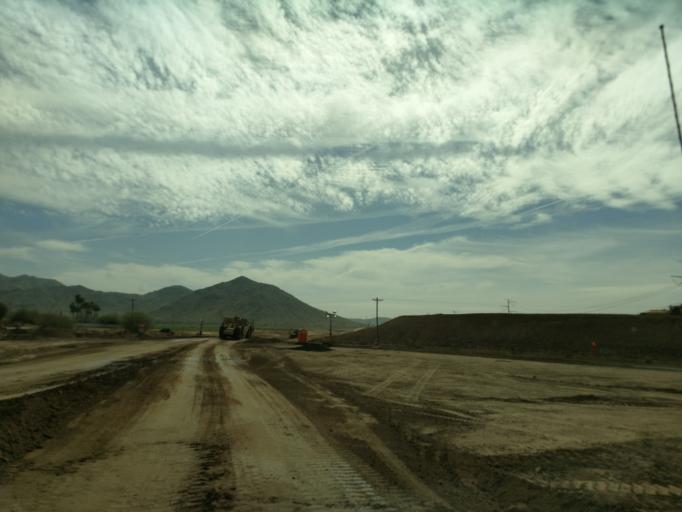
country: US
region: Arizona
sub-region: Maricopa County
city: Laveen
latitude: 33.3345
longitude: -112.1764
